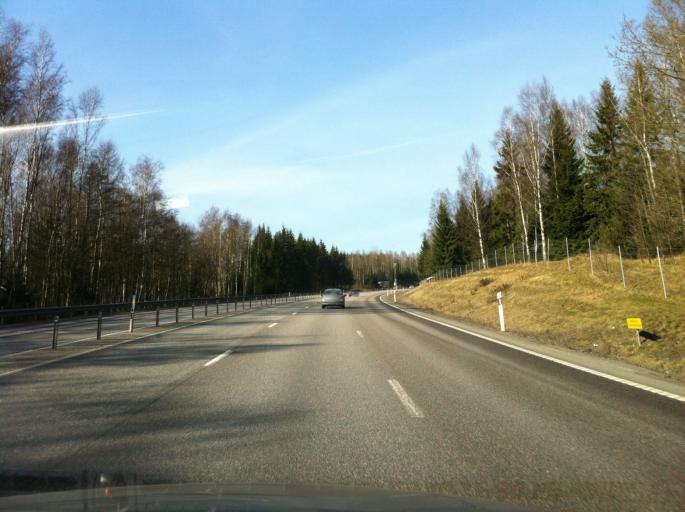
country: SE
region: Joenkoeping
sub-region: Jonkopings Kommun
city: Jonkoping
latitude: 57.7498
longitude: 14.1187
